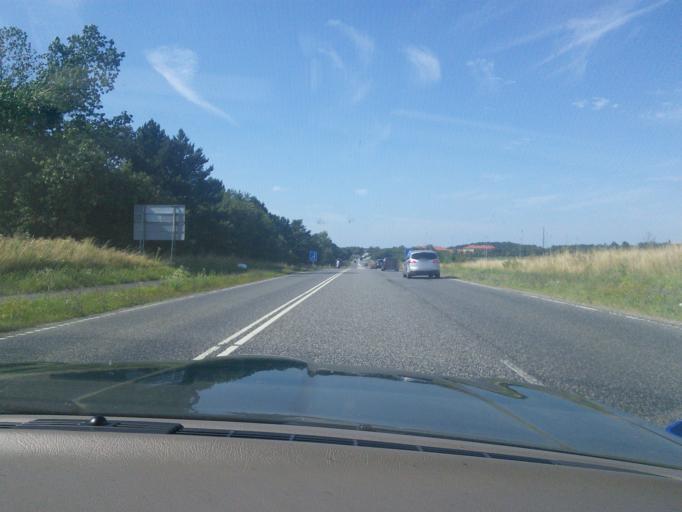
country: DK
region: Capital Region
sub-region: Halsnaes Kommune
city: Frederiksvaerk
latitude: 55.9582
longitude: 12.0357
